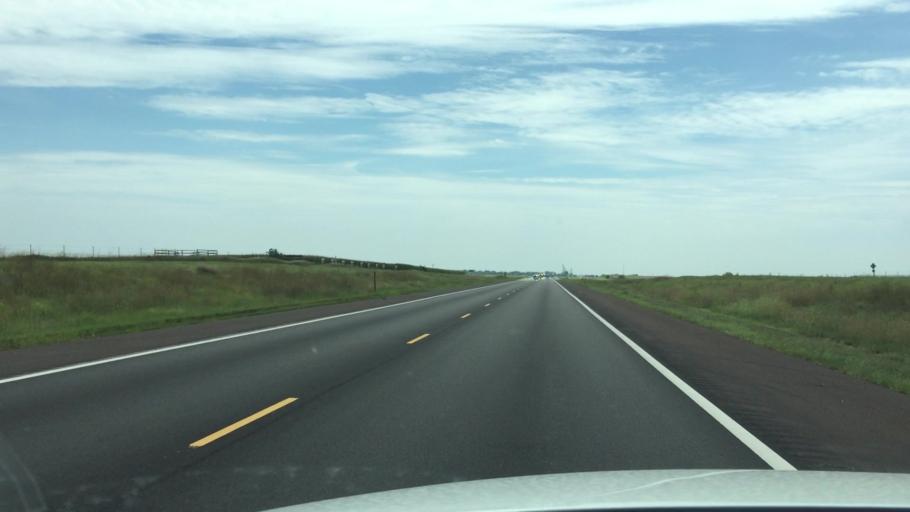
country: US
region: Kansas
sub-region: Nemaha County
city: Sabetha
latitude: 39.8563
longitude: -95.7559
